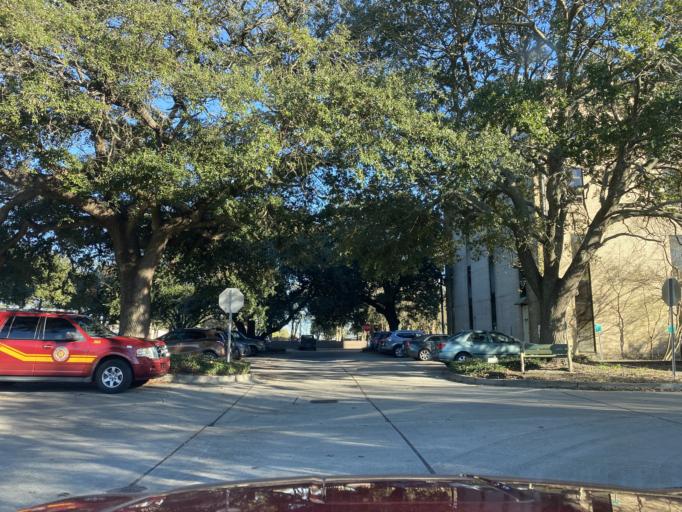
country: US
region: Louisiana
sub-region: Jefferson Parish
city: Kenner
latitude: 29.9907
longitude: -90.2431
